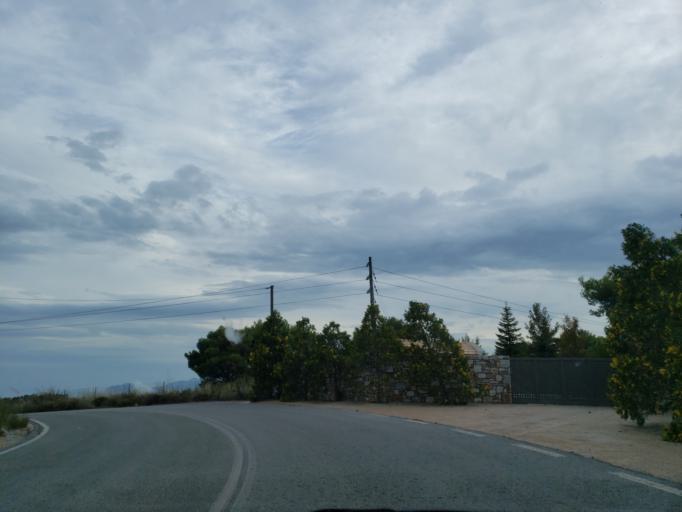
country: GR
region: Attica
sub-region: Nomarchia Anatolikis Attikis
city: Varnavas
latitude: 38.2172
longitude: 23.9397
